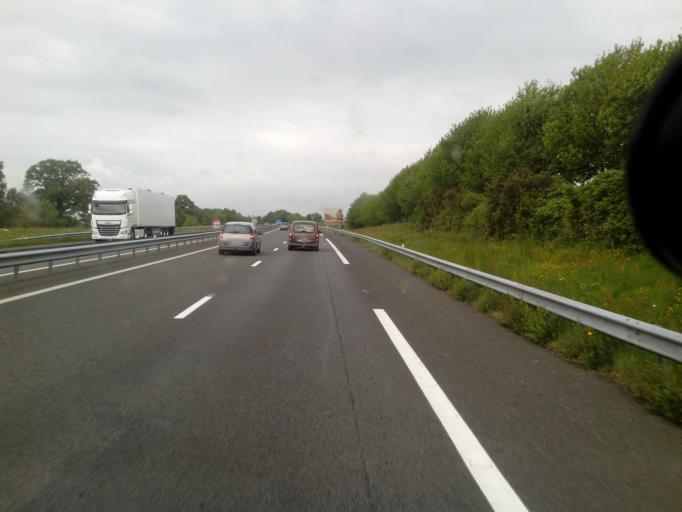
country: FR
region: Brittany
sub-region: Departement d'Ille-et-Vilaine
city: Saint-Etienne-en-Cogles
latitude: 48.4189
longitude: -1.3121
